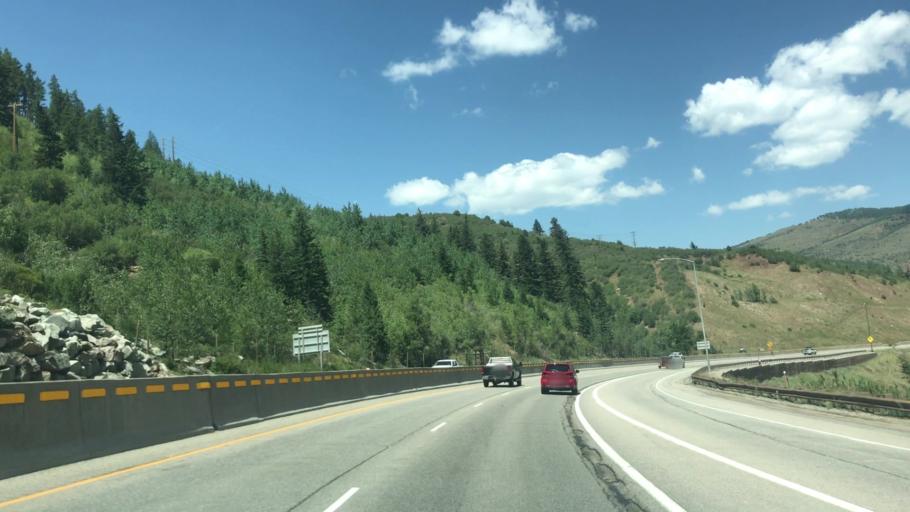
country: US
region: Colorado
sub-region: Eagle County
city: Minturn
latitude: 39.6105
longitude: -106.4577
